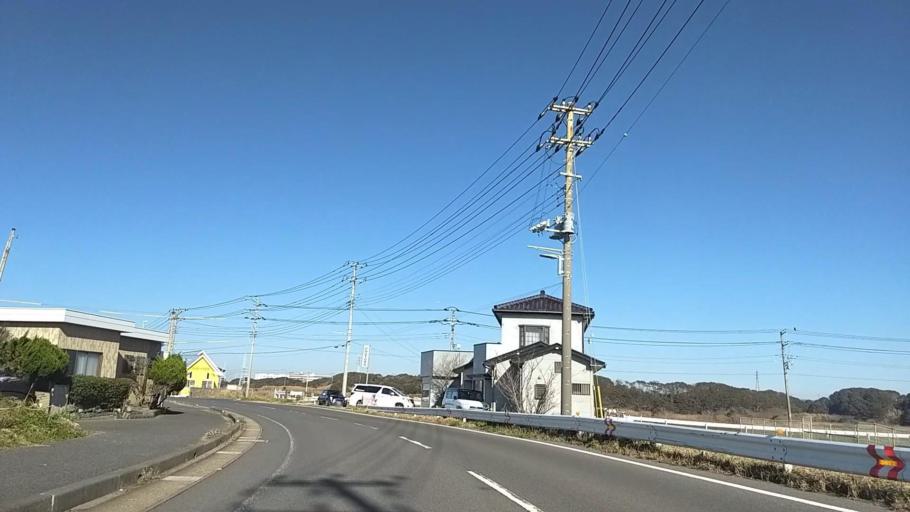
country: JP
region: Chiba
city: Hasaki
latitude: 35.7138
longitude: 140.8409
